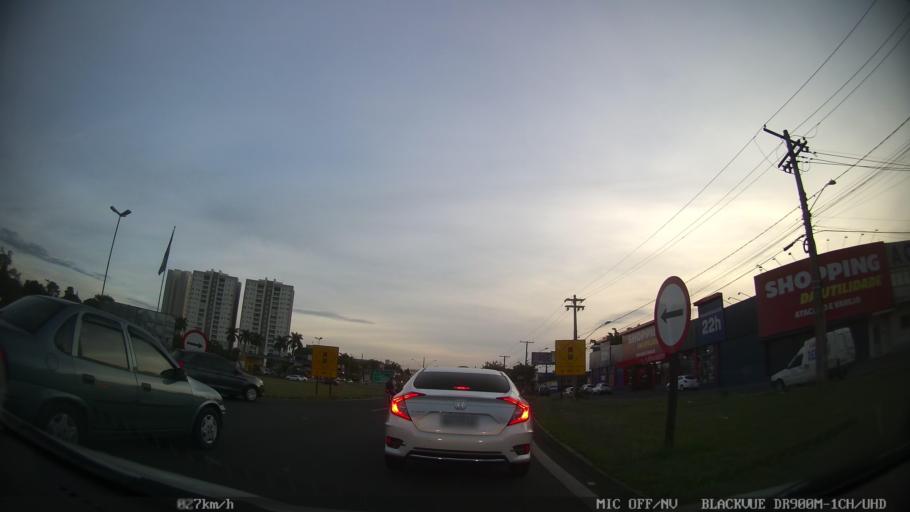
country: BR
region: Sao Paulo
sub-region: Limeira
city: Limeira
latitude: -22.5618
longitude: -47.4176
